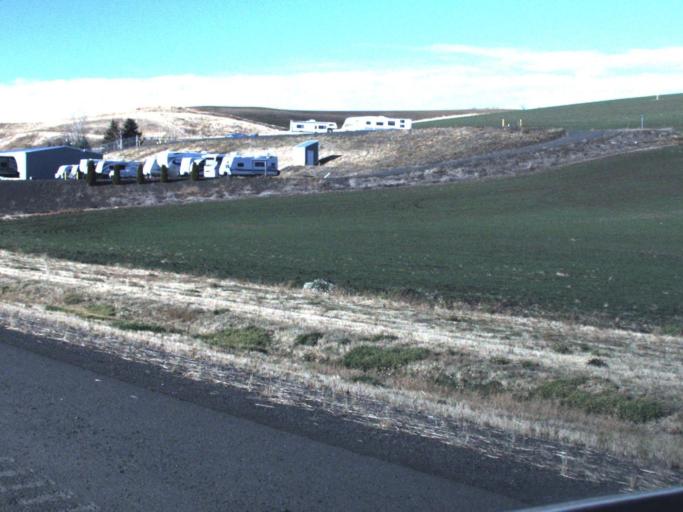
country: US
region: Washington
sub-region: Whitman County
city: Pullman
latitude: 46.7299
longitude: -117.0953
